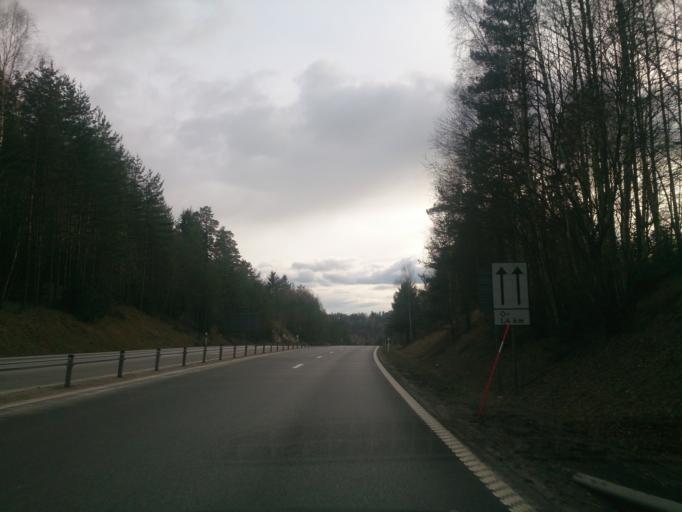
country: SE
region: OEstergoetland
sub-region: Norrkopings Kommun
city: Jursla
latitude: 58.6906
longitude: 16.1562
